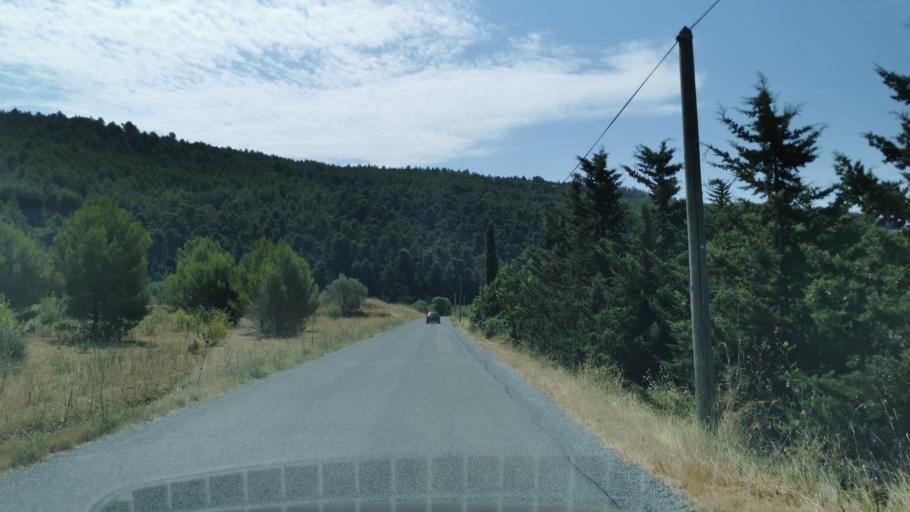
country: FR
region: Languedoc-Roussillon
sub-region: Departement de l'Aude
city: Bize-Minervois
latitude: 43.3244
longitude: 2.8801
